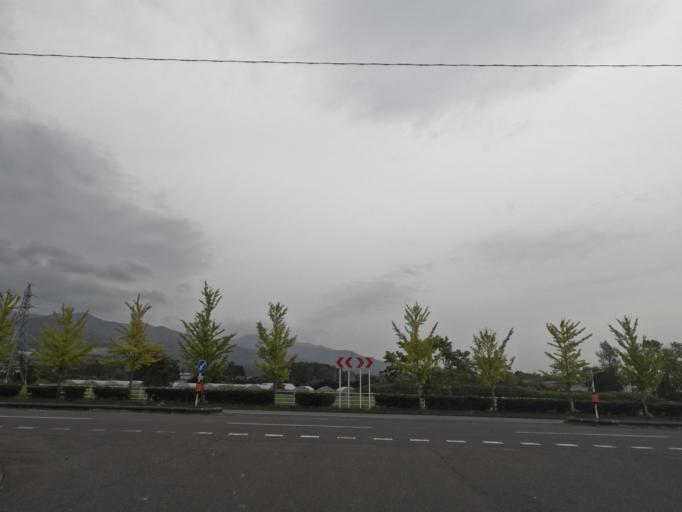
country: JP
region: Hokkaido
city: Date
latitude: 42.4769
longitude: 140.8851
